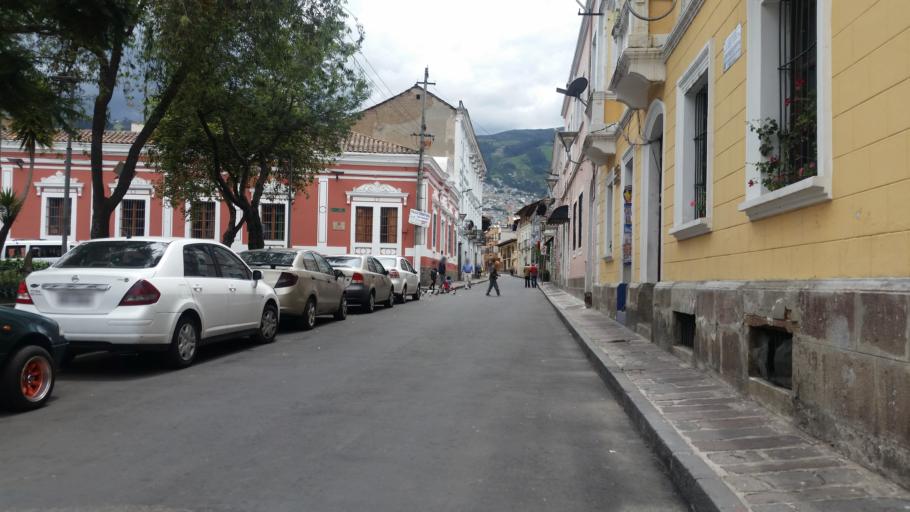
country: EC
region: Pichincha
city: Quito
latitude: -0.2242
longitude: -78.5086
